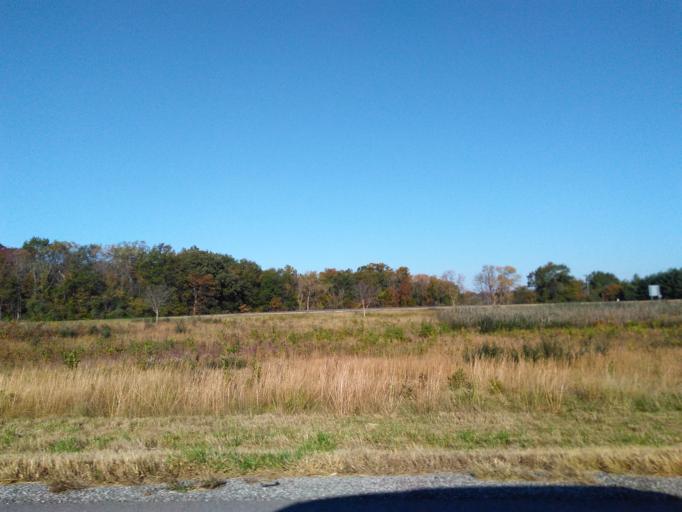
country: US
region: Illinois
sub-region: Madison County
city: Saint Jacob
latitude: 38.7756
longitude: -89.7441
